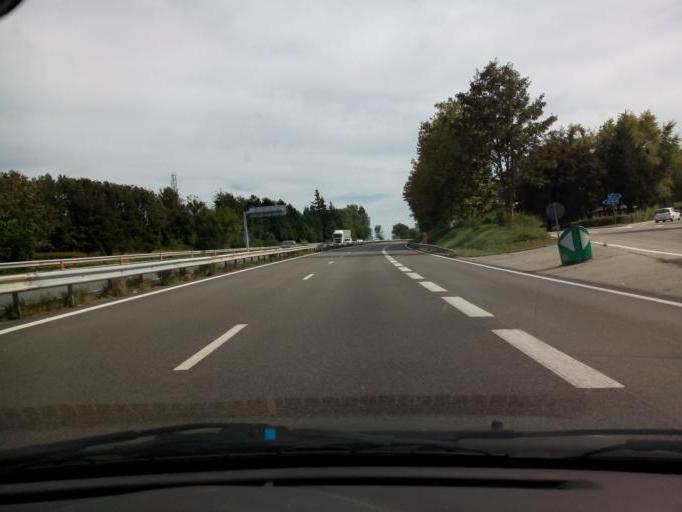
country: FR
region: Rhone-Alpes
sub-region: Departement de l'Isere
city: Saint-Victor-de-Cessieu
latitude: 45.5317
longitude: 5.4076
